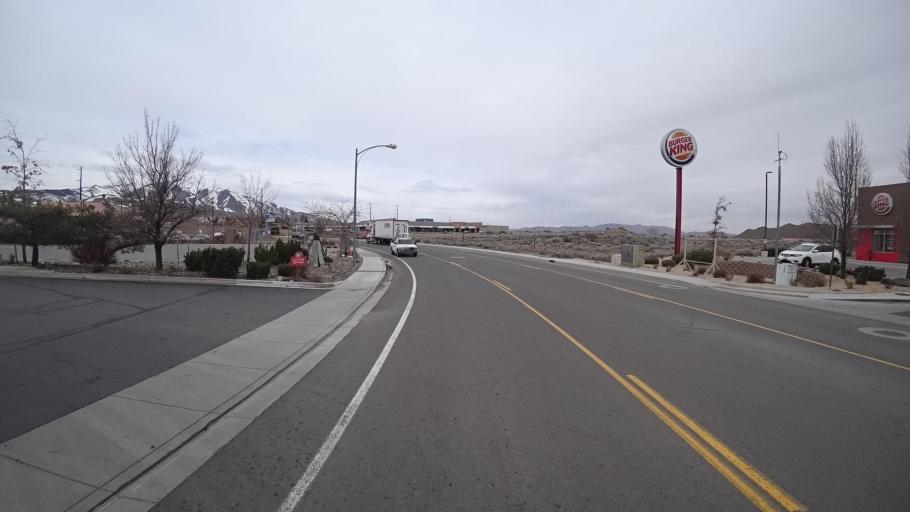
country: US
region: Nevada
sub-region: Washoe County
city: Golden Valley
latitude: 39.6044
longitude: -119.8370
